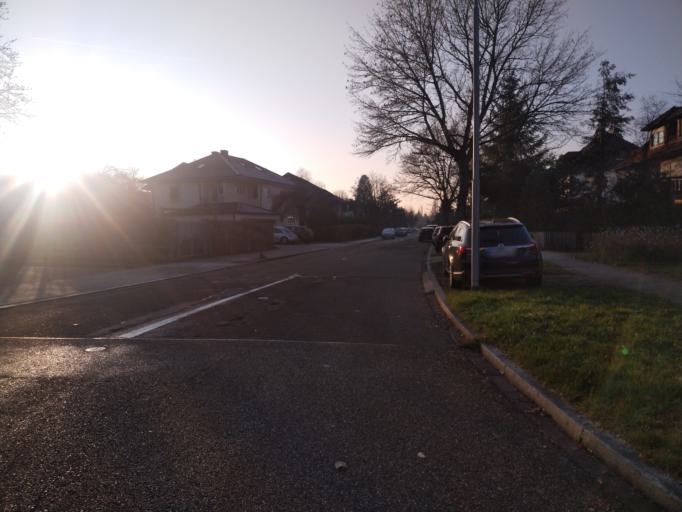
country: DE
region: Baden-Wuerttemberg
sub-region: Karlsruhe Region
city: Pforzheim
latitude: 48.8870
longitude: 8.6863
